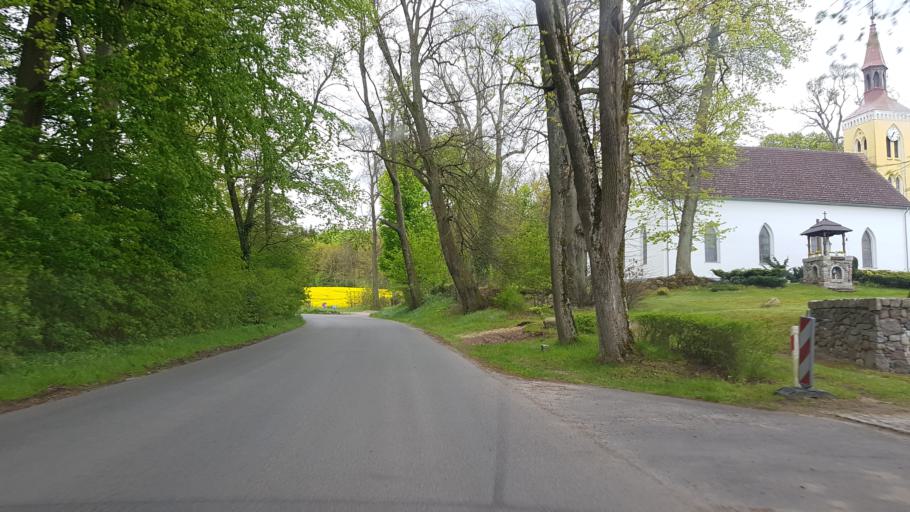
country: PL
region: West Pomeranian Voivodeship
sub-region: Powiat slawienski
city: Slawno
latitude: 54.2719
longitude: 16.5512
